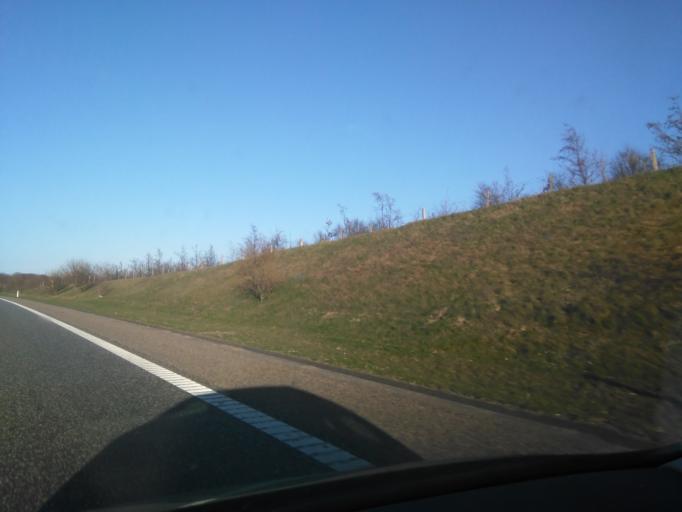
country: DK
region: Central Jutland
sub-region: Skanderborg Kommune
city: Skovby
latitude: 56.1422
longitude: 9.9501
